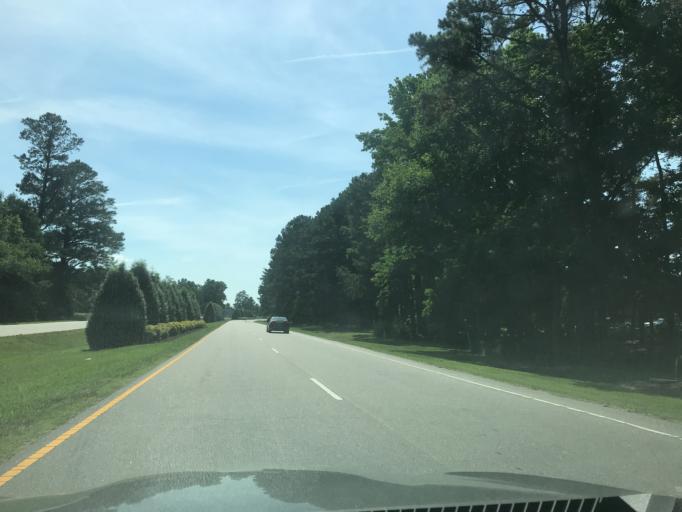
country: US
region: North Carolina
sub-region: Wake County
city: Wendell
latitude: 35.8030
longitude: -78.4134
